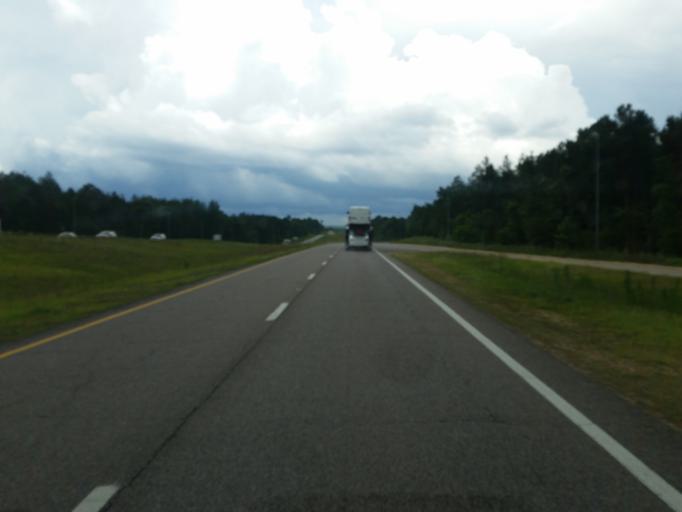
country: US
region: Mississippi
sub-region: George County
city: Lucedale
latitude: 30.8884
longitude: -88.4457
